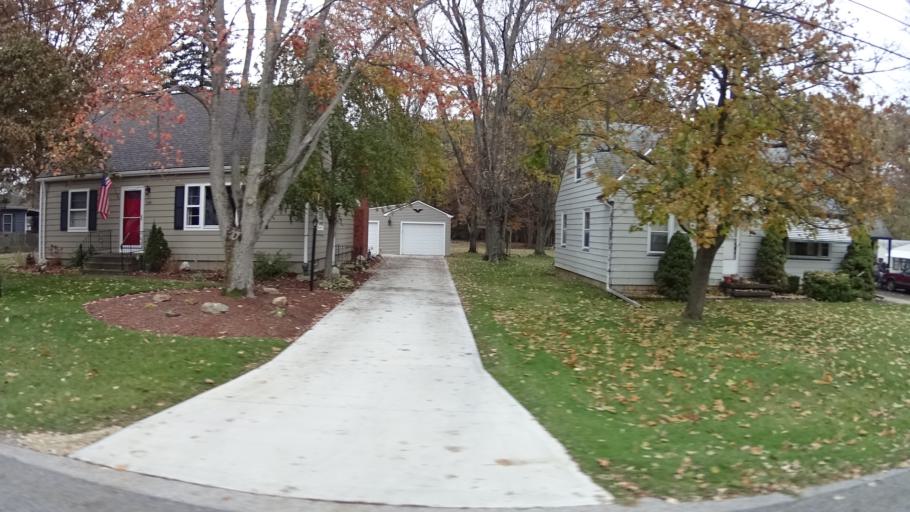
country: US
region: Ohio
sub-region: Lorain County
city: Elyria
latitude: 41.3315
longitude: -82.0755
